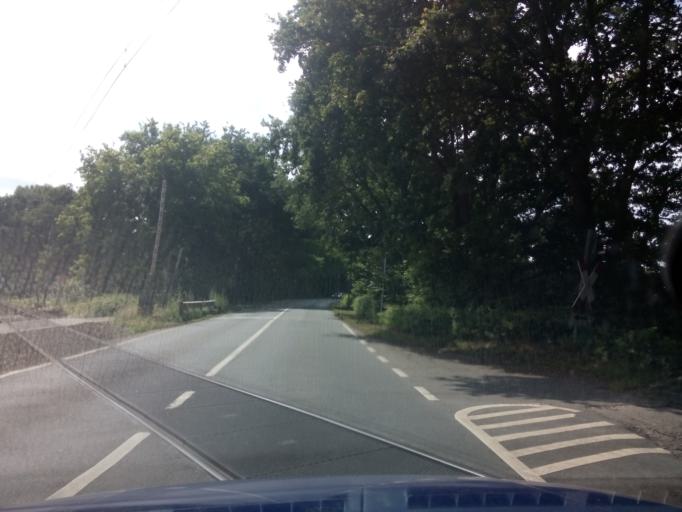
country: DE
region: Lower Saxony
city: Osterholz-Scharmbeck
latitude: 53.2410
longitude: 8.8063
